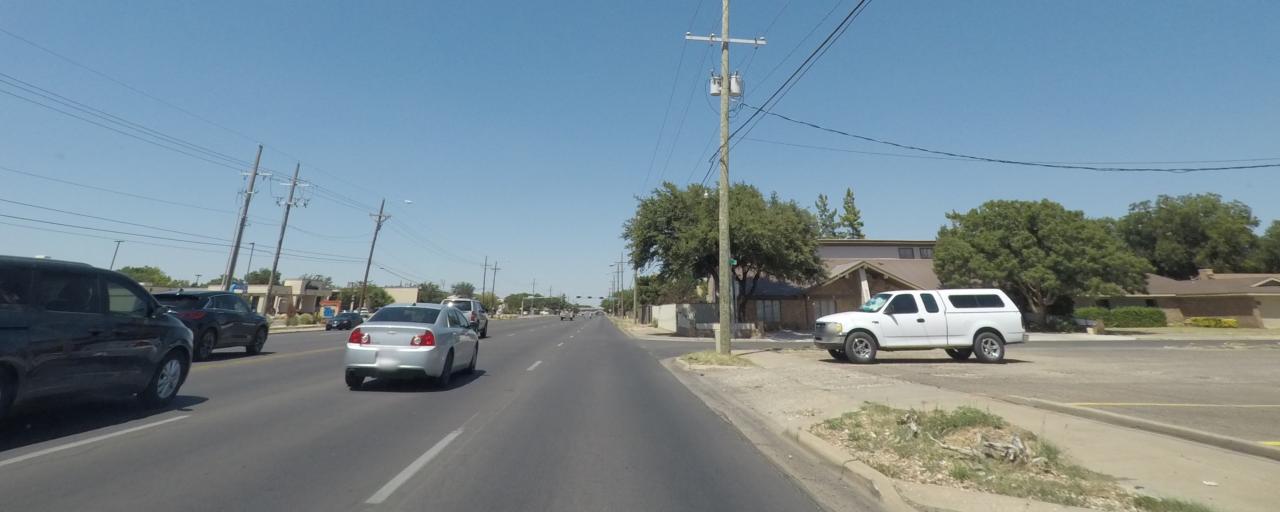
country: US
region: Texas
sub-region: Lubbock County
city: Lubbock
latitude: 33.5207
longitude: -101.8876
